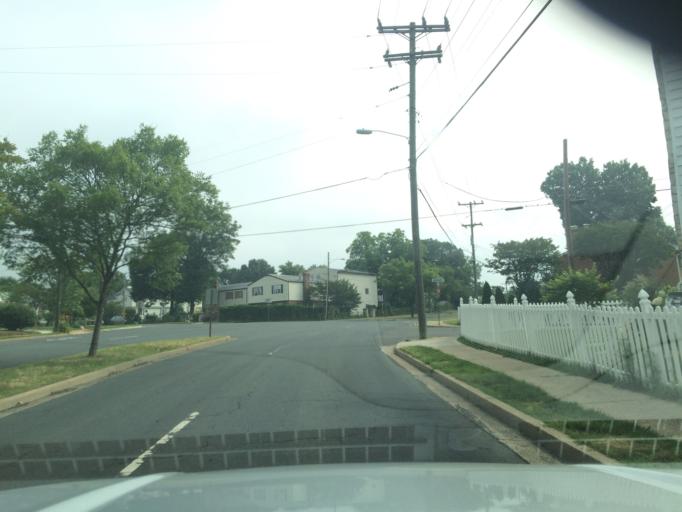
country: US
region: Virginia
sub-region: Arlington County
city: Arlington
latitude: 38.8522
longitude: -77.0910
